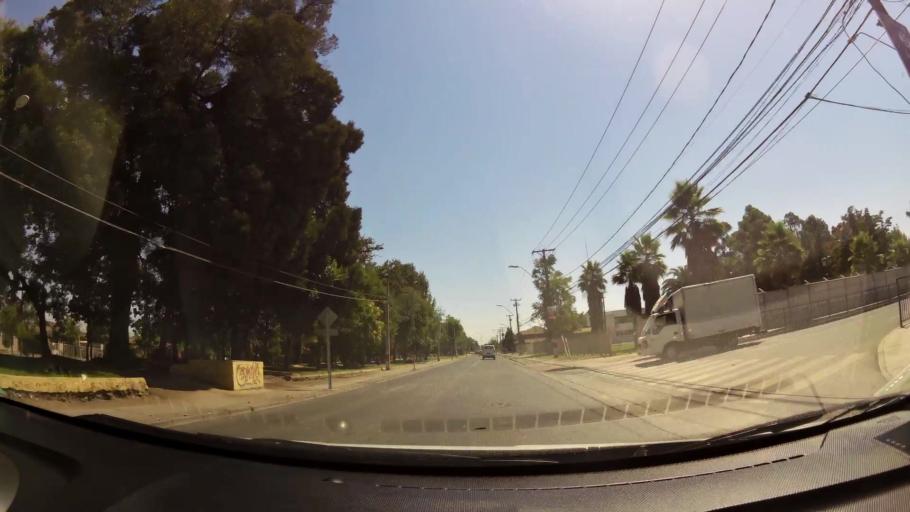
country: CL
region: Maule
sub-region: Provincia de Curico
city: Curico
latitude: -34.9727
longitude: -71.2313
